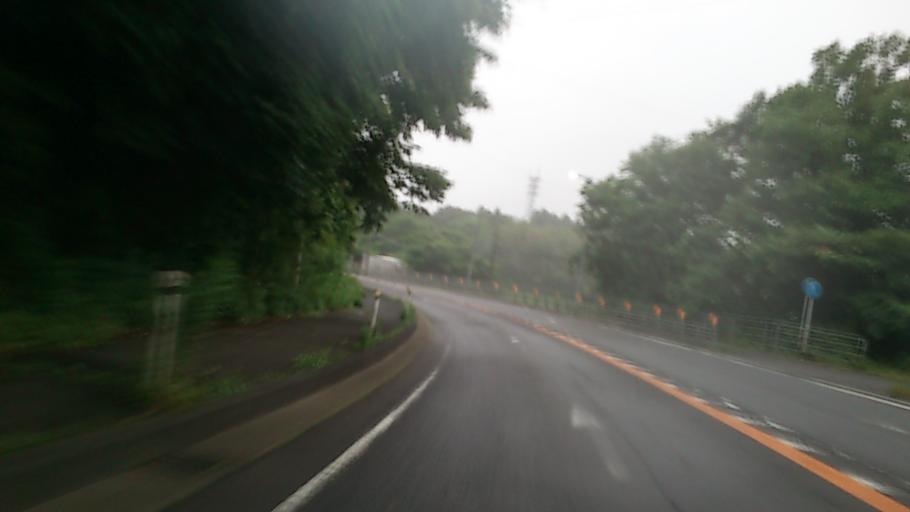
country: JP
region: Tochigi
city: Kuroiso
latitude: 37.0578
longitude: 140.1070
